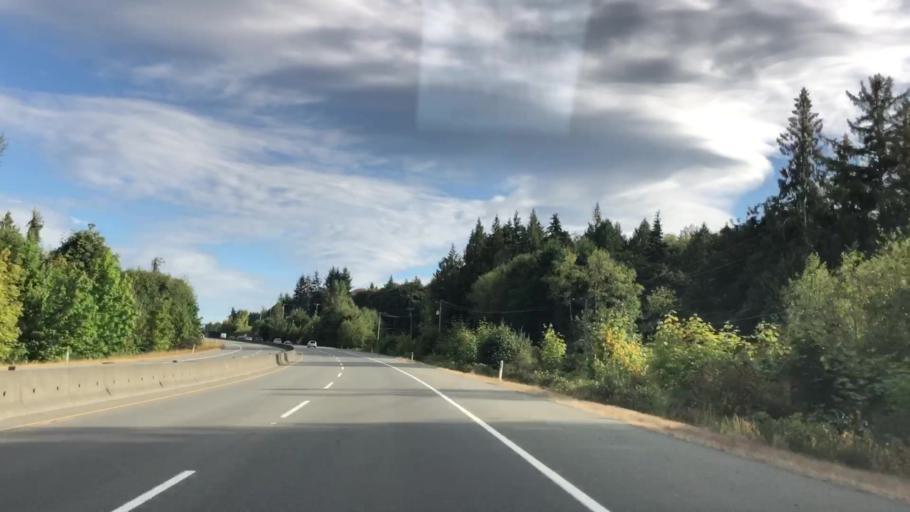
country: CA
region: British Columbia
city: North Saanich
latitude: 48.6496
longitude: -123.5596
